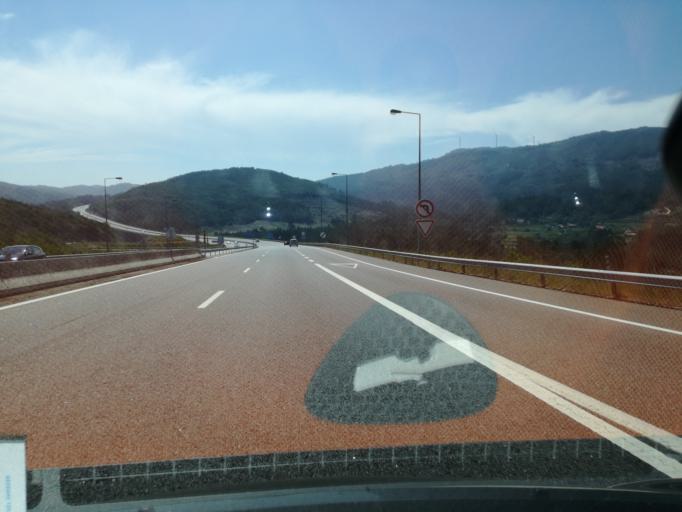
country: PT
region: Viana do Castelo
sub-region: Caminha
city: Vila Praia de Ancora
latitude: 41.8057
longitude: -8.8032
